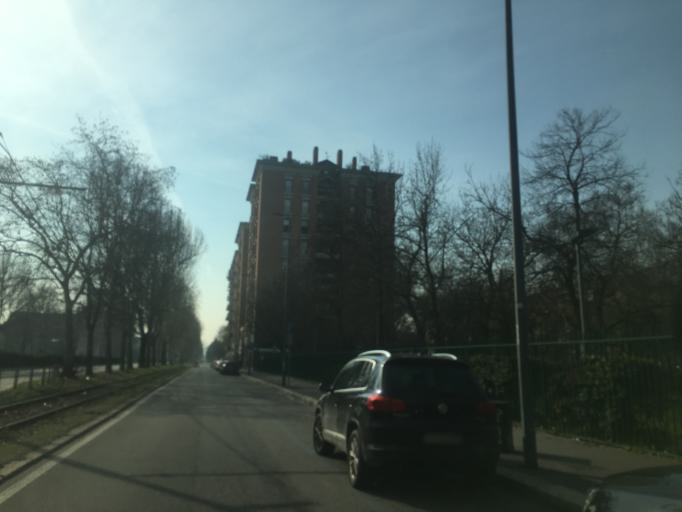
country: IT
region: Lombardy
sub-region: Citta metropolitana di Milano
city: Bresso
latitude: 45.5182
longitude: 9.2069
